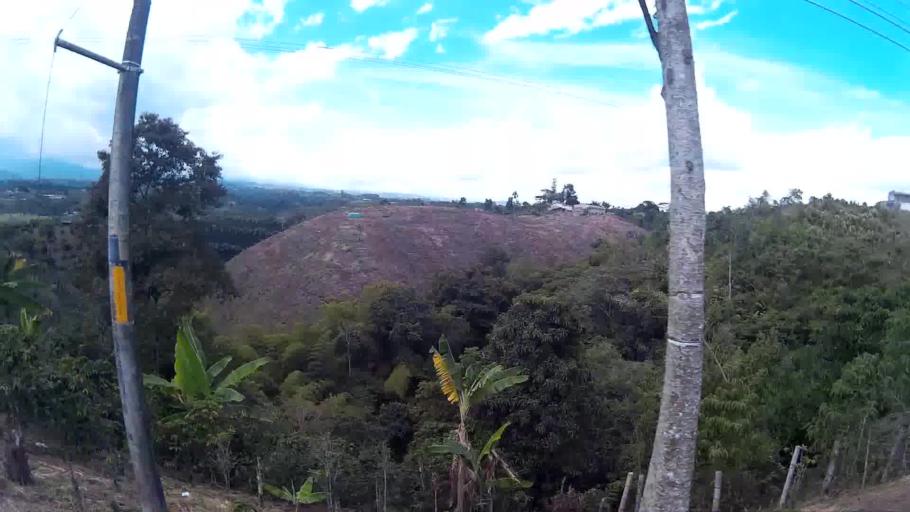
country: CO
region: Valle del Cauca
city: Ulloa
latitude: 4.7501
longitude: -75.7143
